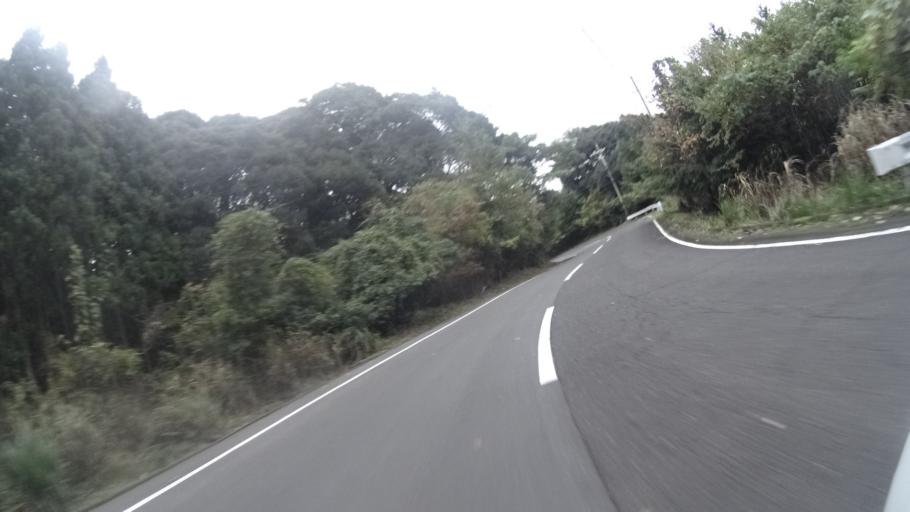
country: JP
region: Kyoto
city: Maizuru
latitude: 35.5677
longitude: 135.4510
